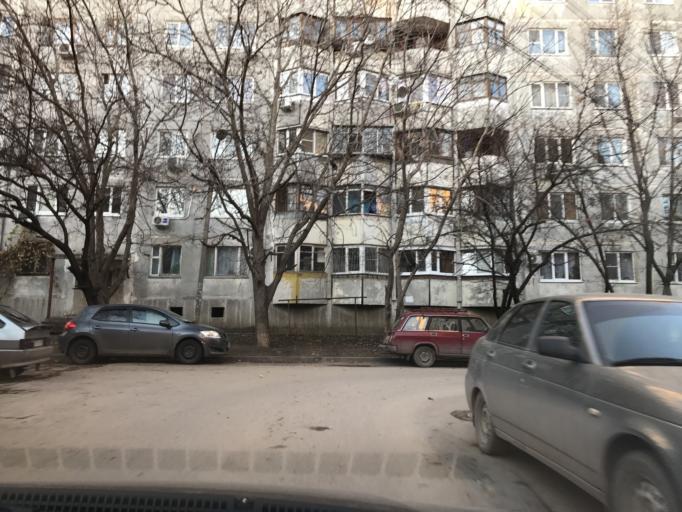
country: RU
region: Rostov
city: Rostov-na-Donu
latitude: 47.2312
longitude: 39.6212
